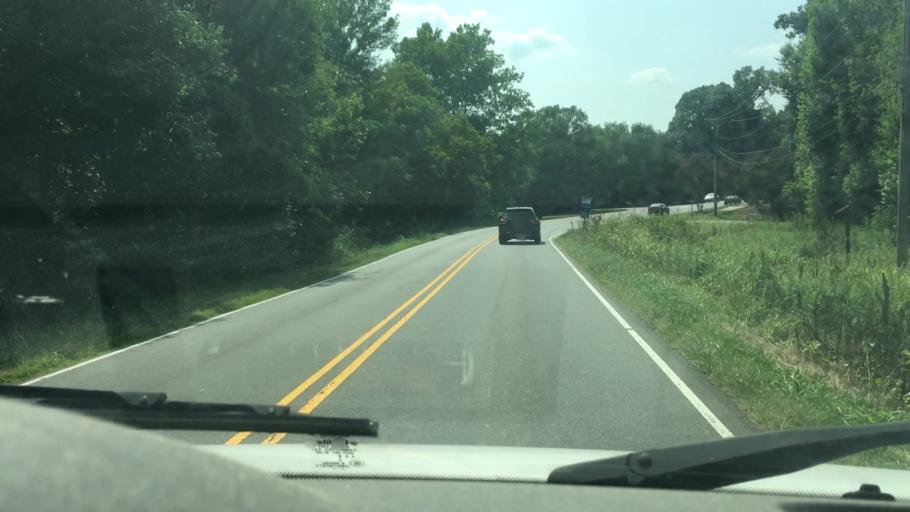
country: US
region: North Carolina
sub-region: Mecklenburg County
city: Huntersville
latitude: 35.4042
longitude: -80.8807
